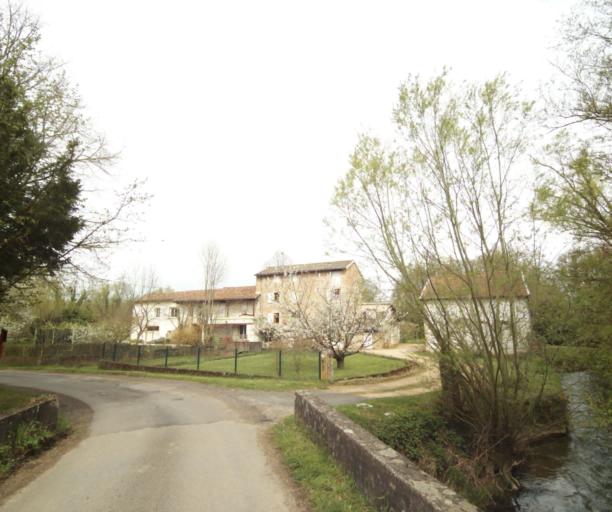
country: FR
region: Bourgogne
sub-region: Departement de Saone-et-Loire
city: Charnay-les-Macon
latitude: 46.3069
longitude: 4.7640
